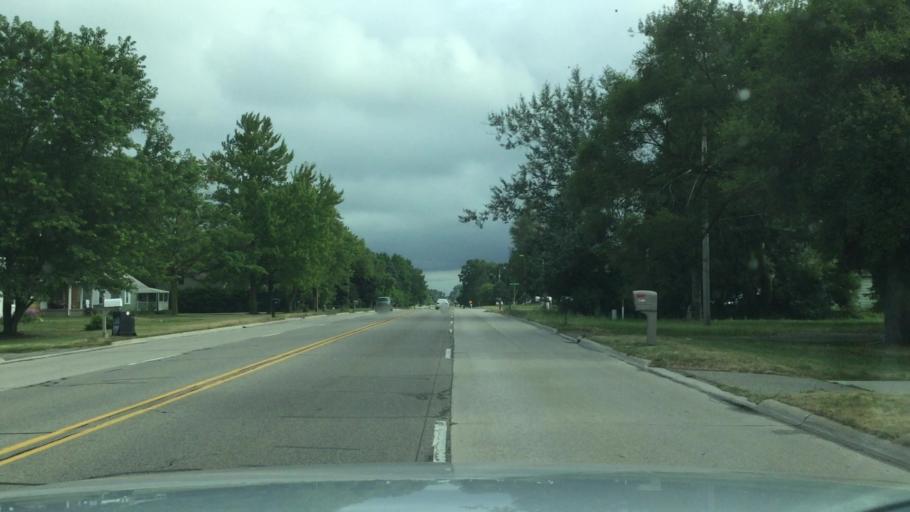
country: US
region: Michigan
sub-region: Genesee County
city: Burton
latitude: 43.0589
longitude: -83.6164
